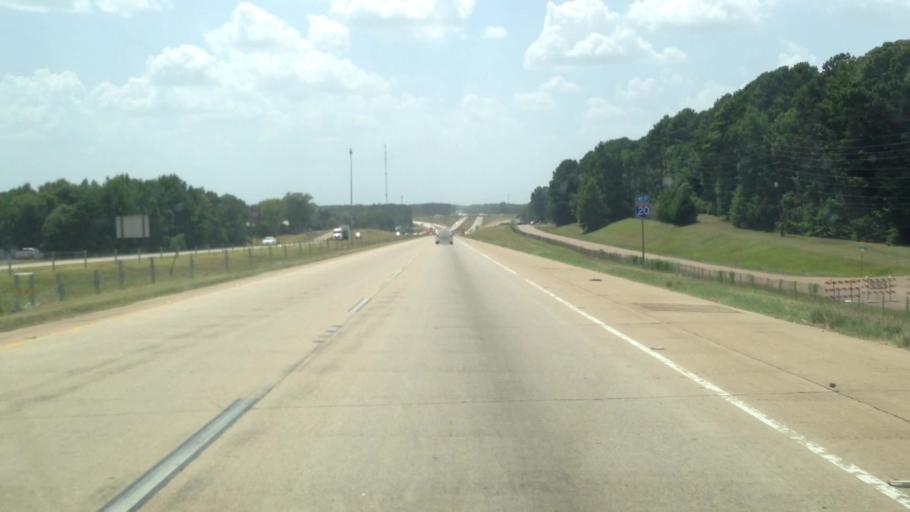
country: US
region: Louisiana
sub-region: Lincoln Parish
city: Ruston
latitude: 32.5403
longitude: -92.6605
